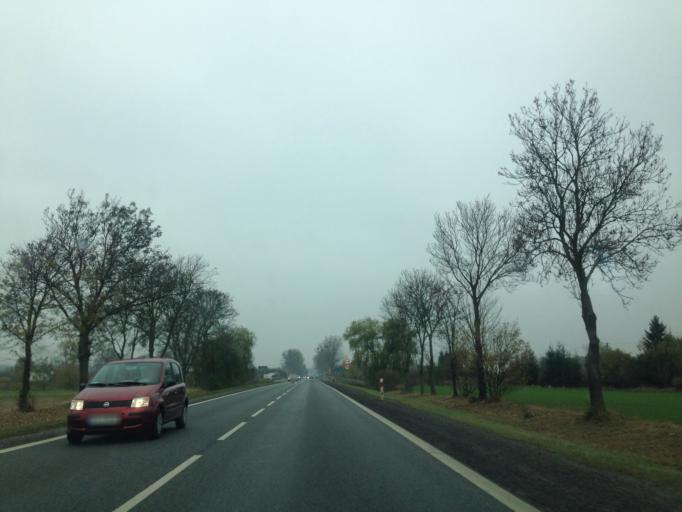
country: PL
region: Kujawsko-Pomorskie
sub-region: Grudziadz
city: Grudziadz
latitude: 53.4946
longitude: 18.7004
